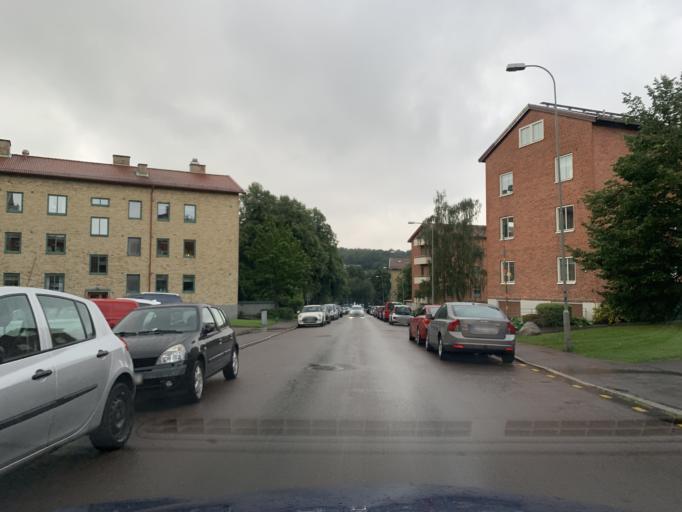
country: SE
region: Vaestra Goetaland
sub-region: Molndal
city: Moelndal
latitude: 57.7028
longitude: 12.0168
